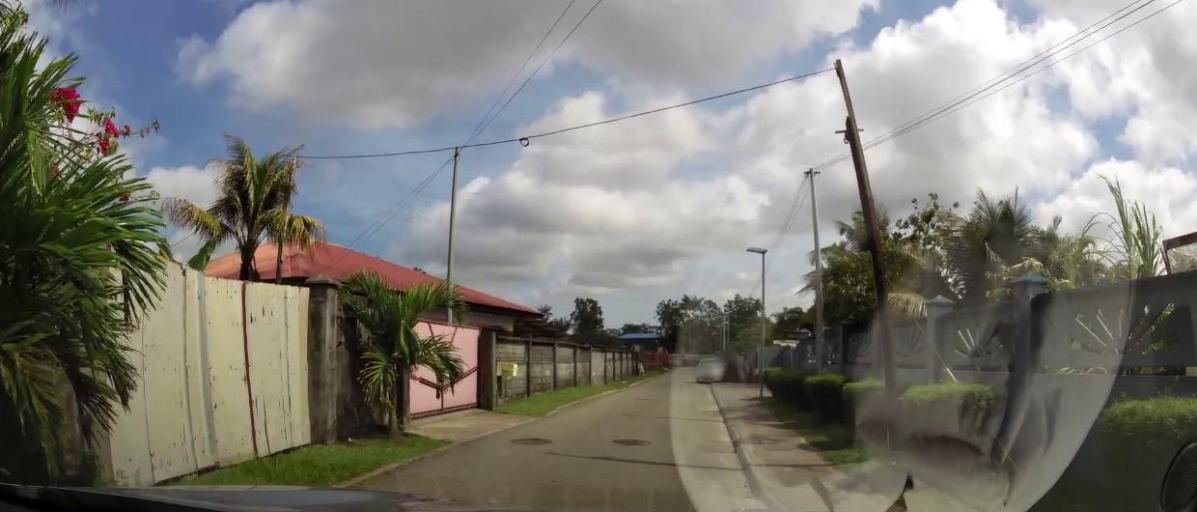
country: GF
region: Guyane
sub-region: Guyane
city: Matoury
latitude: 4.8761
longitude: -52.3272
